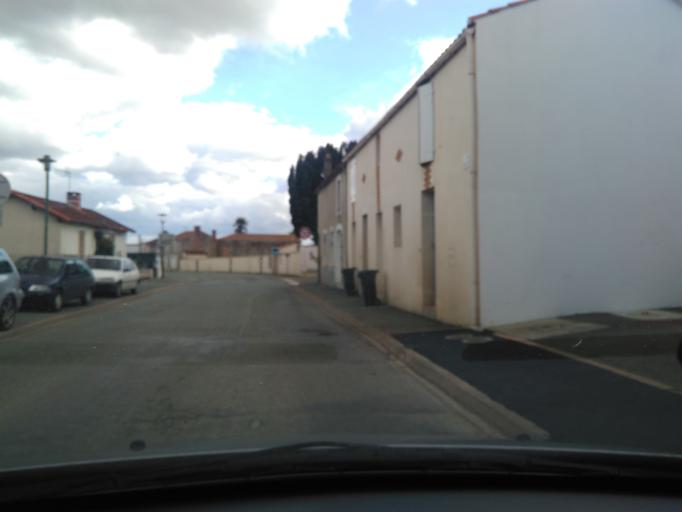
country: FR
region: Pays de la Loire
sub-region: Departement de la Vendee
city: Sainte-Cecile
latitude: 46.6884
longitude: -1.1299
